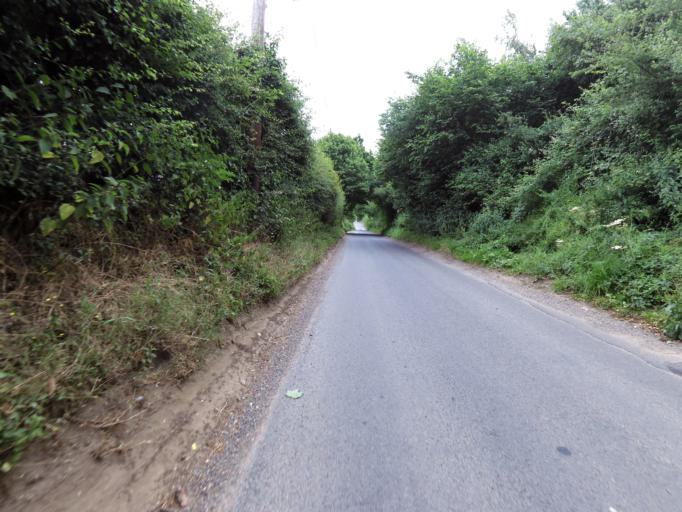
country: GB
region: England
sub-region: Norfolk
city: Harleston
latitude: 52.3989
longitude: 1.2337
